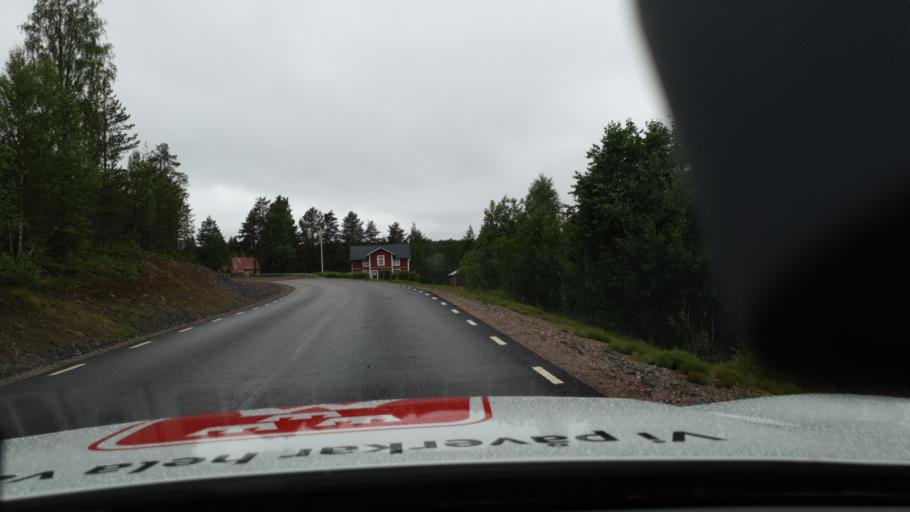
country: SE
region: Norrbotten
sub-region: Overtornea Kommun
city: OEvertornea
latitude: 66.4205
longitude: 23.5664
